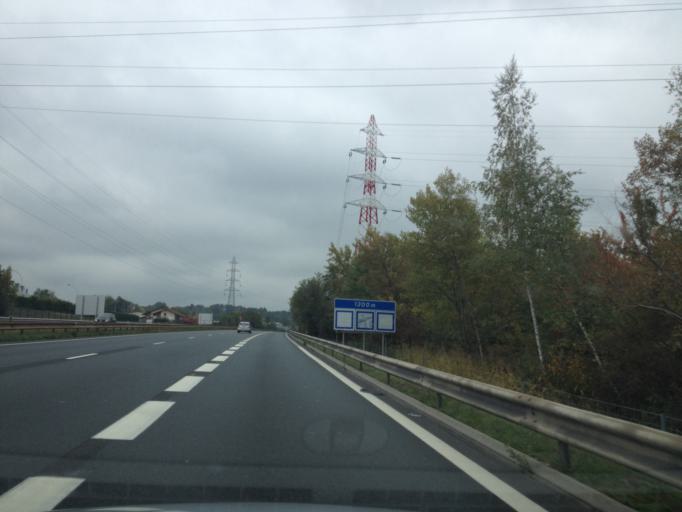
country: FR
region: Rhone-Alpes
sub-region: Departement de la Haute-Savoie
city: Seynod
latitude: 45.8897
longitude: 6.0845
